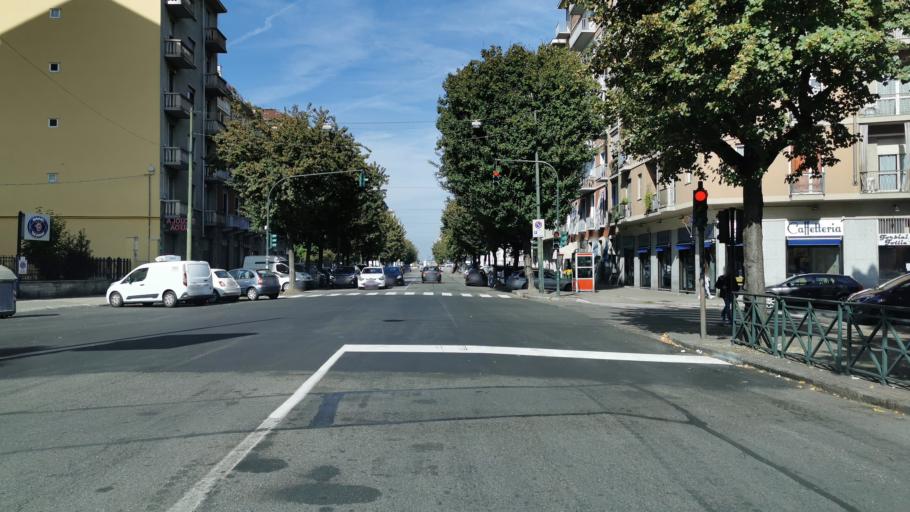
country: IT
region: Piedmont
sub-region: Provincia di Torino
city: Turin
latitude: 45.1002
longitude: 7.6631
